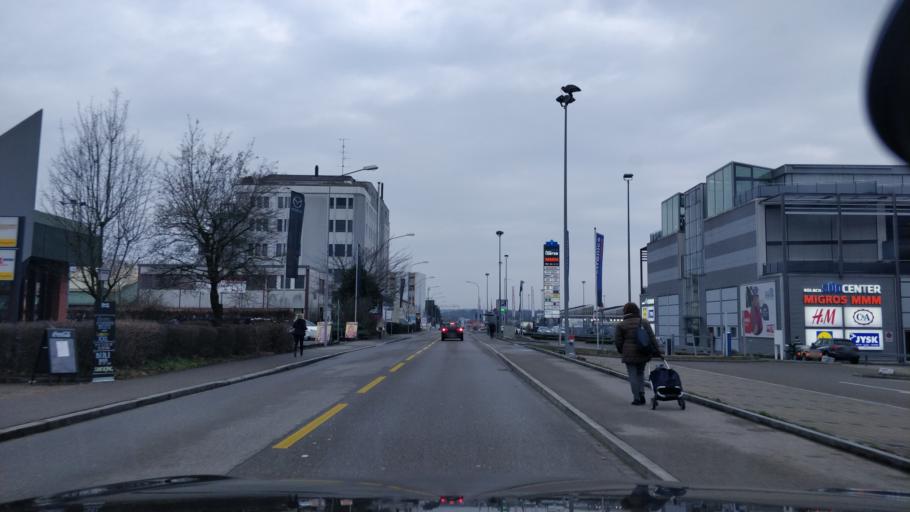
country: CH
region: Zurich
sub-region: Bezirk Buelach
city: Bachenbulach
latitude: 47.5083
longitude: 8.5406
